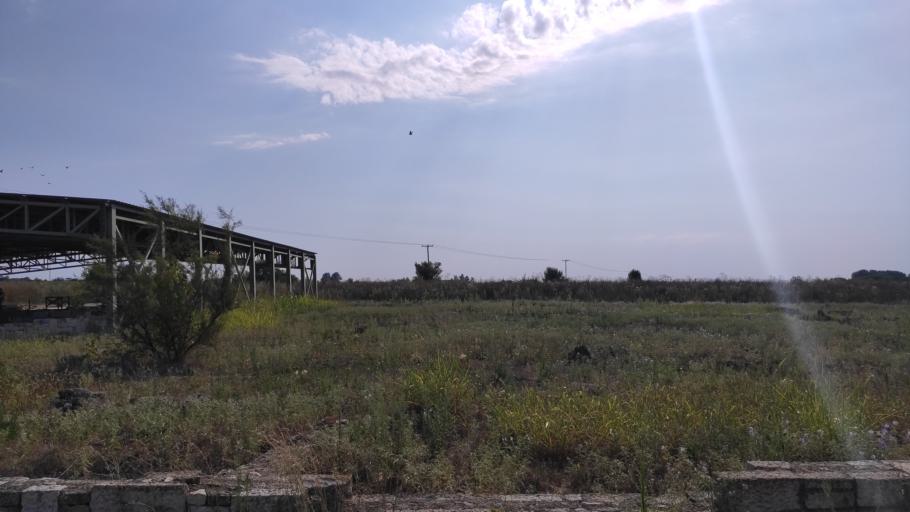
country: GR
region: Central Macedonia
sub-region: Nomos Pellis
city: Pella
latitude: 40.7520
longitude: 22.5179
